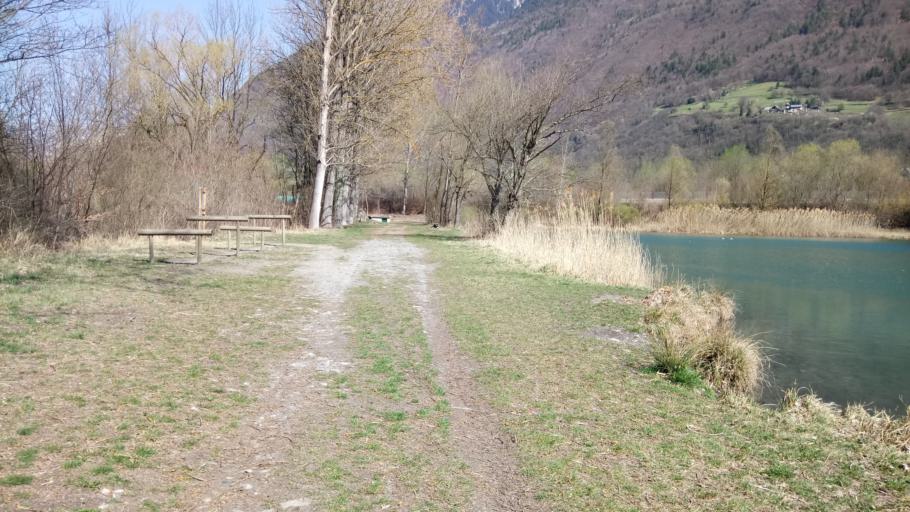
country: FR
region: Rhone-Alpes
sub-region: Departement de la Savoie
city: Saint-Remy-de-Maurienne
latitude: 45.3959
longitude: 6.2721
